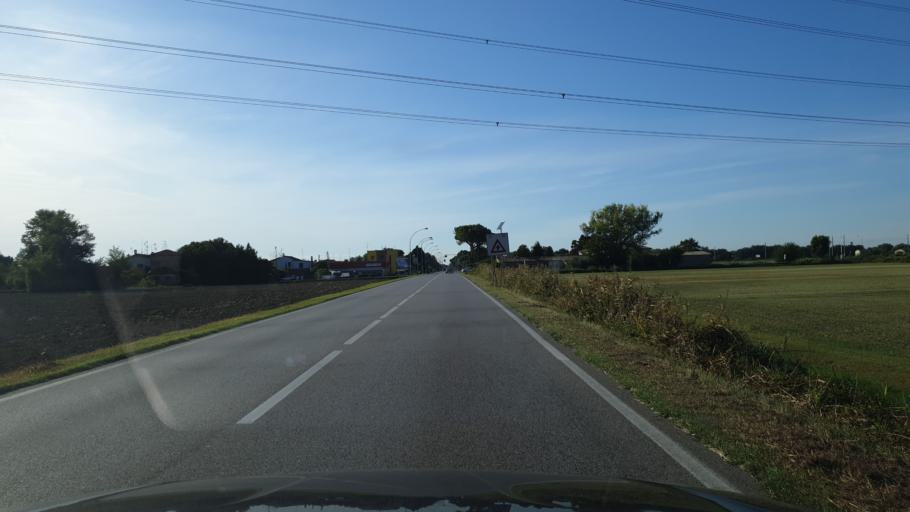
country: IT
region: Emilia-Romagna
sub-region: Provincia di Ravenna
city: Fornace Zarattini
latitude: 44.4466
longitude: 12.1282
